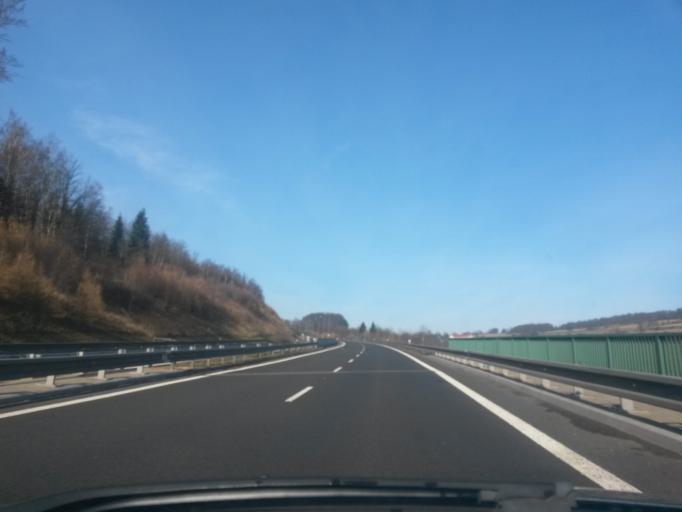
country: CZ
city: Krasna Lipa
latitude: 50.4772
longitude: 13.3447
